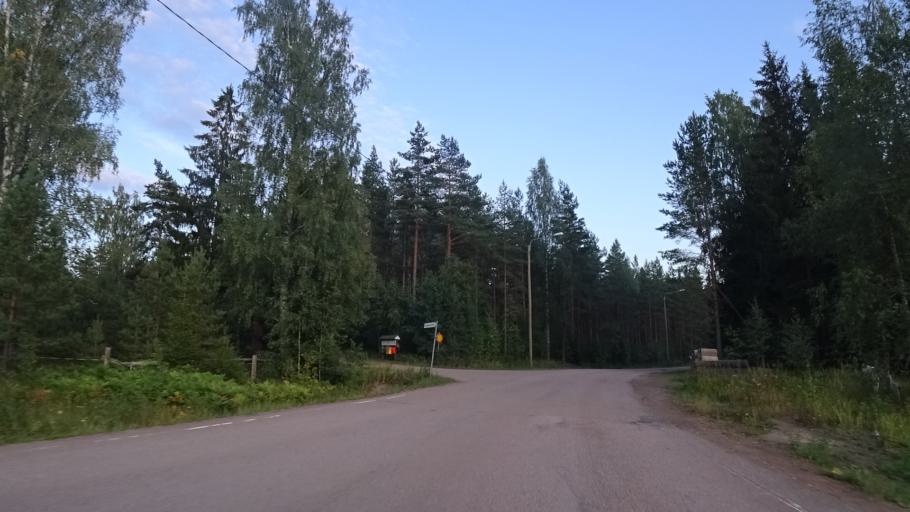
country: FI
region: Kymenlaakso
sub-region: Kotka-Hamina
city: Virojoki
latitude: 60.5928
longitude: 27.7627
